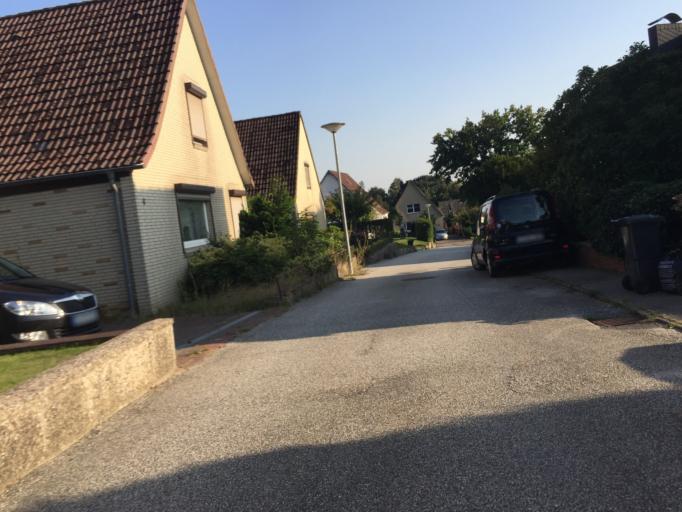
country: DE
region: Schleswig-Holstein
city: Oelixdorf
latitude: 53.9292
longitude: 9.5441
